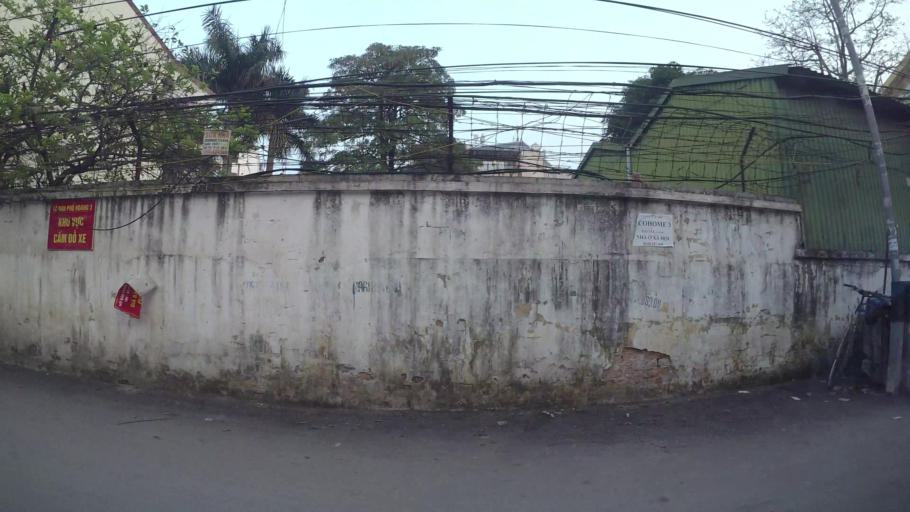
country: VN
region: Ha Noi
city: Cau Giay
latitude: 21.0511
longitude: 105.7899
